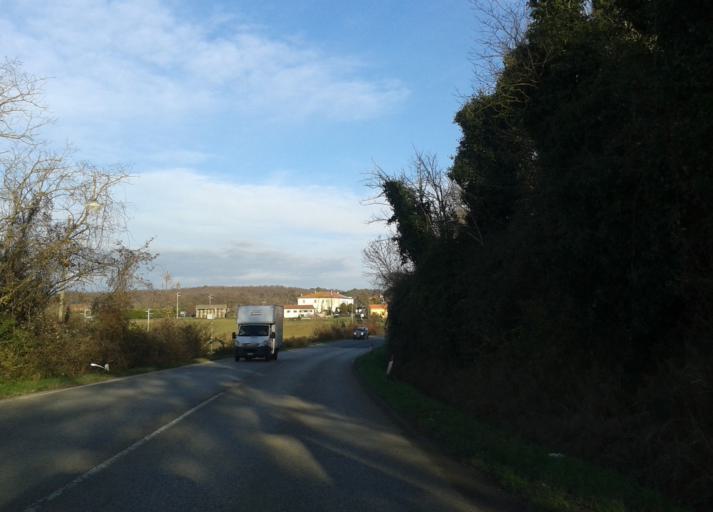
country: IT
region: Tuscany
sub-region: Provincia di Livorno
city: Guasticce
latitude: 43.5724
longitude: 10.3702
